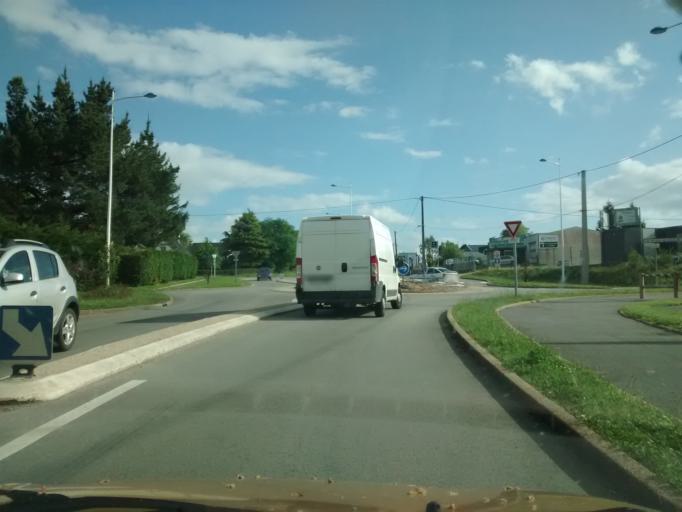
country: FR
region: Brittany
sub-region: Departement du Morbihan
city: Questembert
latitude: 47.6731
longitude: -2.4498
